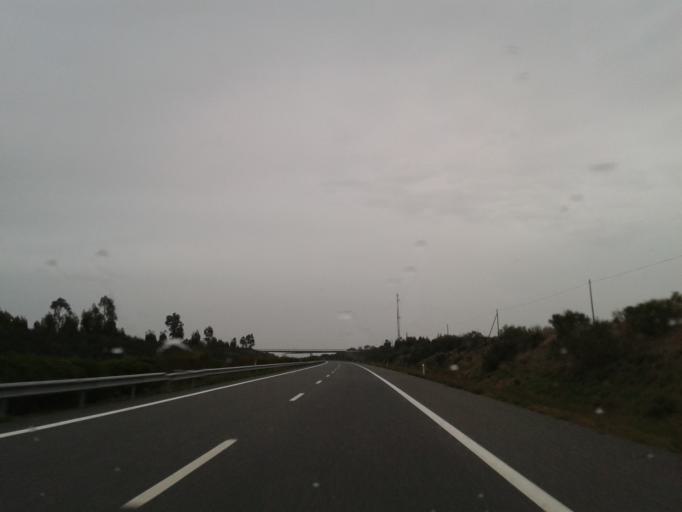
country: PT
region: Beja
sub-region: Ourique
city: Ourique
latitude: 37.6789
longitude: -8.1618
